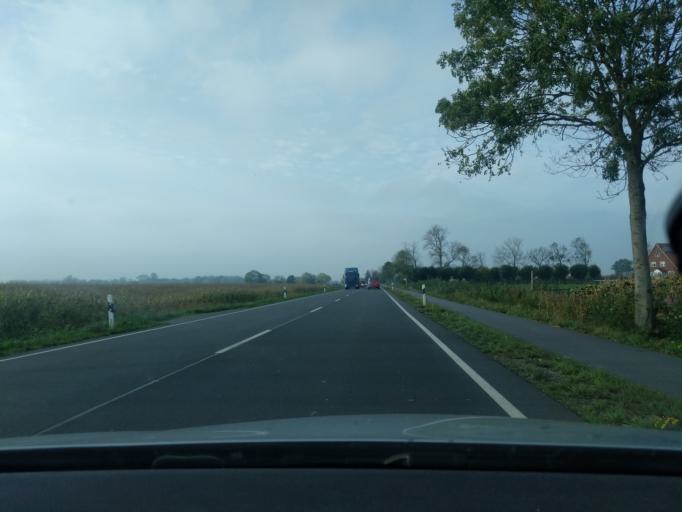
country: DE
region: Lower Saxony
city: Belum
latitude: 53.8210
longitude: 8.9648
